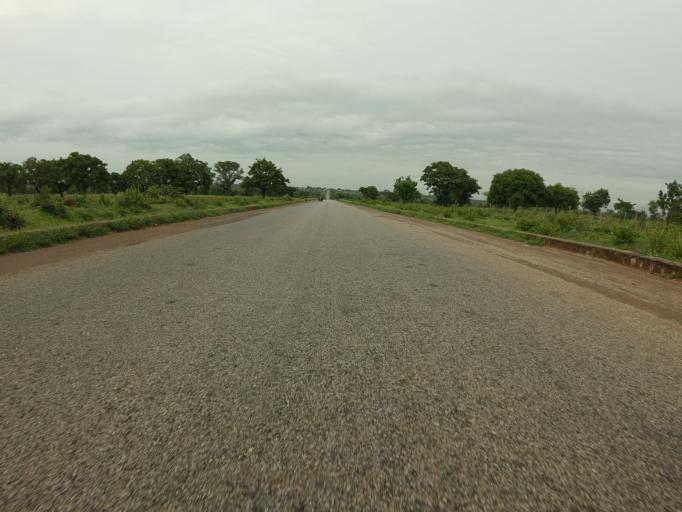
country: GH
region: Northern
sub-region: Yendi
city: Yendi
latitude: 9.5008
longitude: -0.0250
